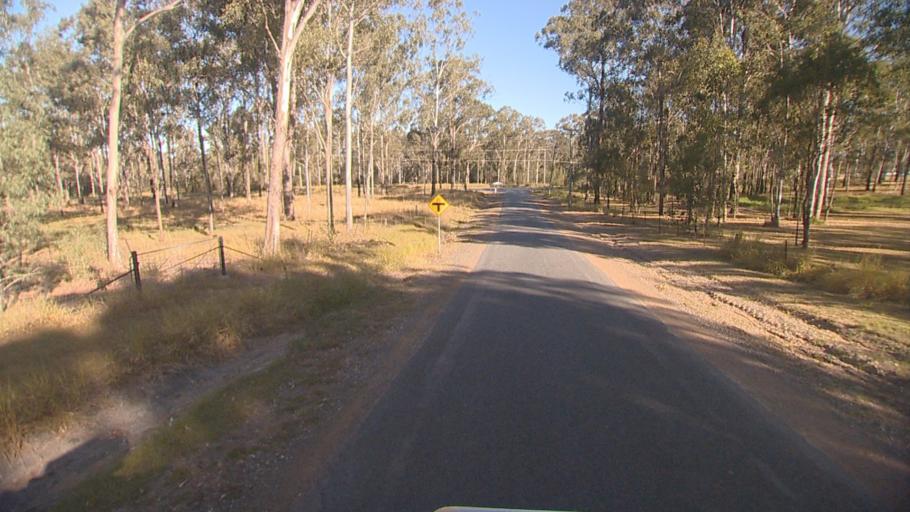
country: AU
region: Queensland
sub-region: Logan
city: North Maclean
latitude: -27.8099
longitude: 153.0333
